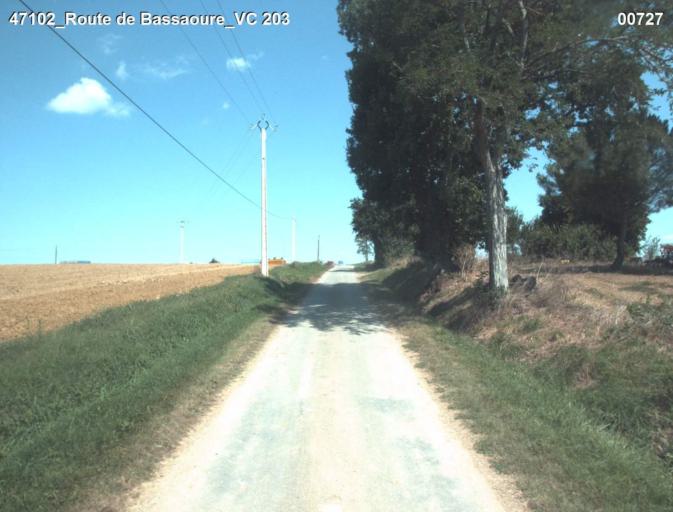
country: FR
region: Aquitaine
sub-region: Departement du Lot-et-Garonne
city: Nerac
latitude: 44.0553
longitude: 0.4295
